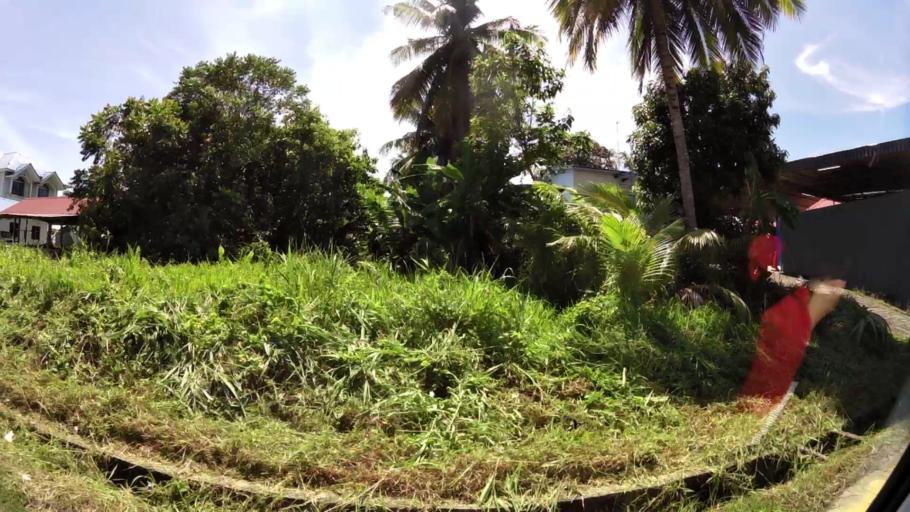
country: BN
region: Brunei and Muara
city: Bandar Seri Begawan
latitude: 4.9422
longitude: 114.9476
